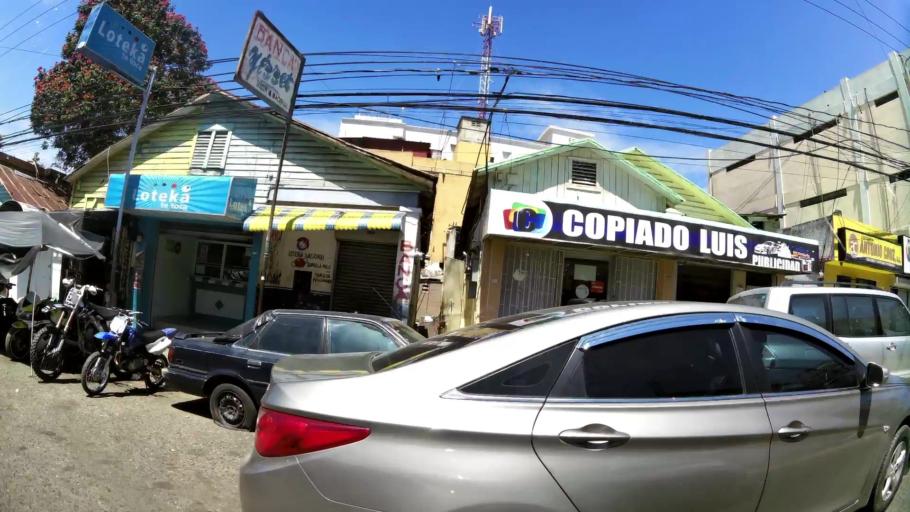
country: DO
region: Santiago
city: Santiago de los Caballeros
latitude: 19.4544
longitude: -70.6987
